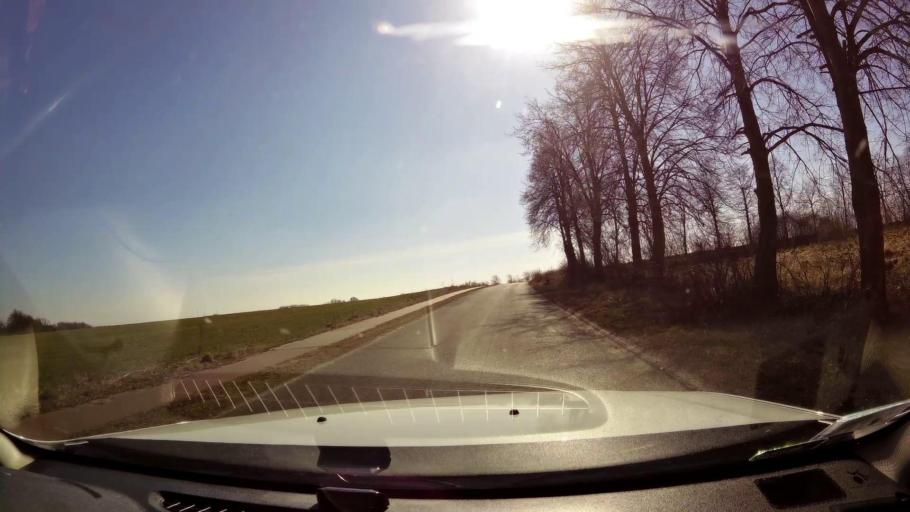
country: PL
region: West Pomeranian Voivodeship
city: Trzcinsko Zdroj
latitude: 52.9830
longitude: 14.6074
